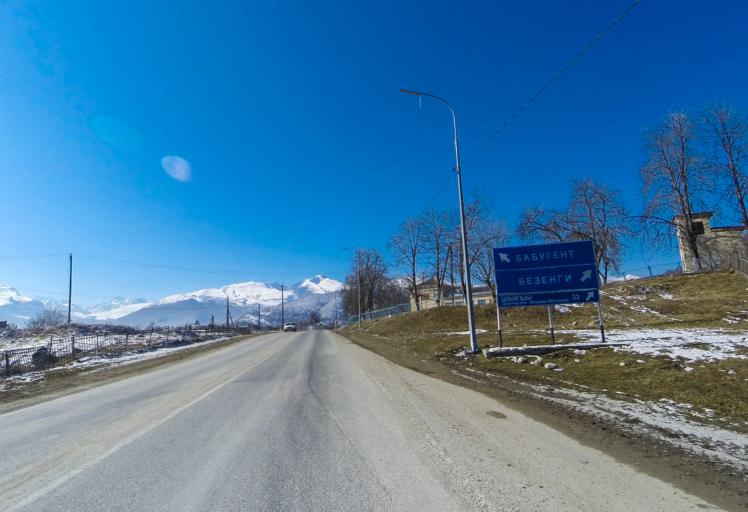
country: RU
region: Kabardino-Balkariya
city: Babugent
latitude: 43.2840
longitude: 43.5569
